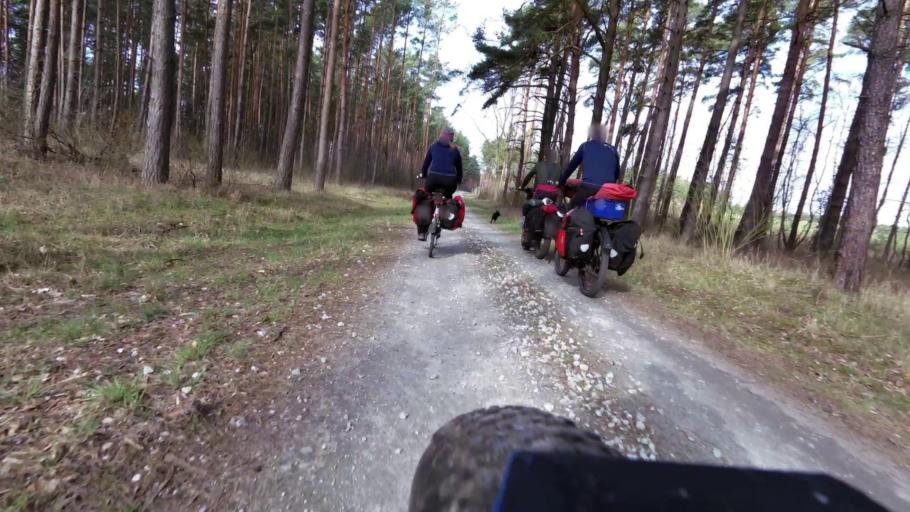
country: DE
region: Brandenburg
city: Ziltendorf
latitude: 52.2807
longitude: 14.6589
